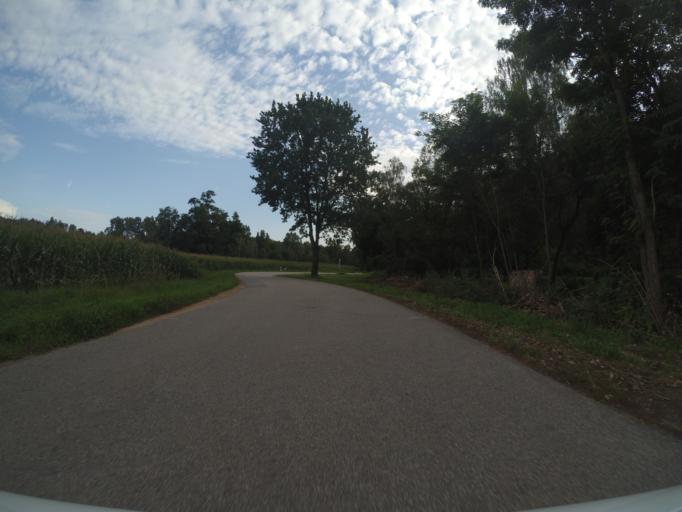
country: DE
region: Bavaria
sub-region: Upper Palatinate
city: Schwarzenfeld
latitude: 49.3939
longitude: 12.1462
